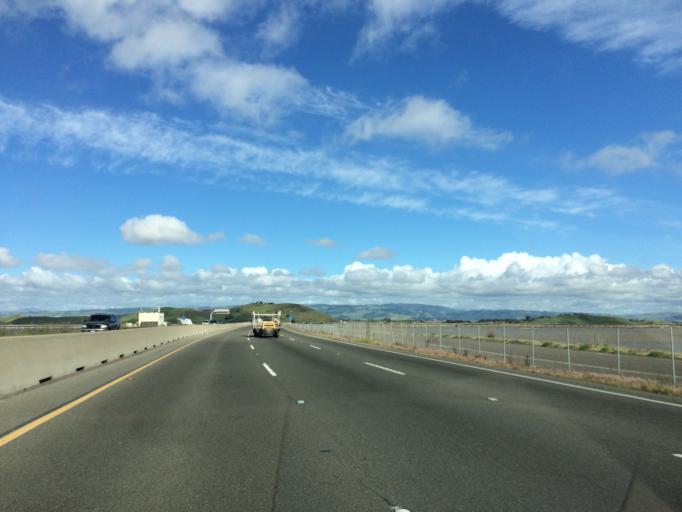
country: US
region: California
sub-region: Alameda County
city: Newark
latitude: 37.5223
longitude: -122.1023
